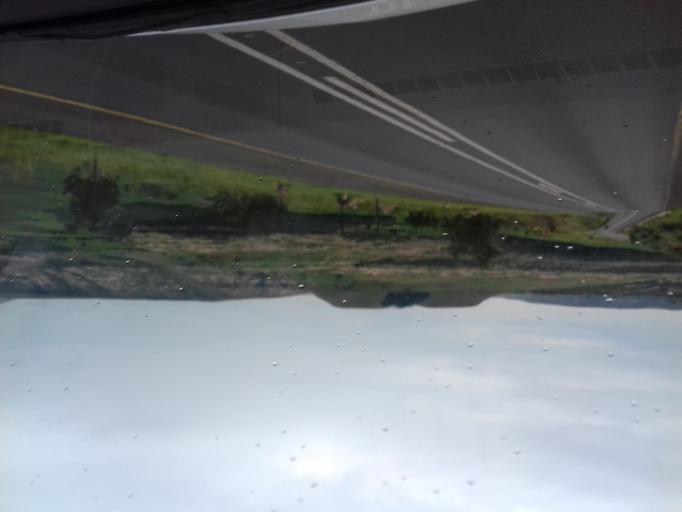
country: LS
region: Leribe
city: Maputsoe
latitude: -29.0944
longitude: 27.9630
